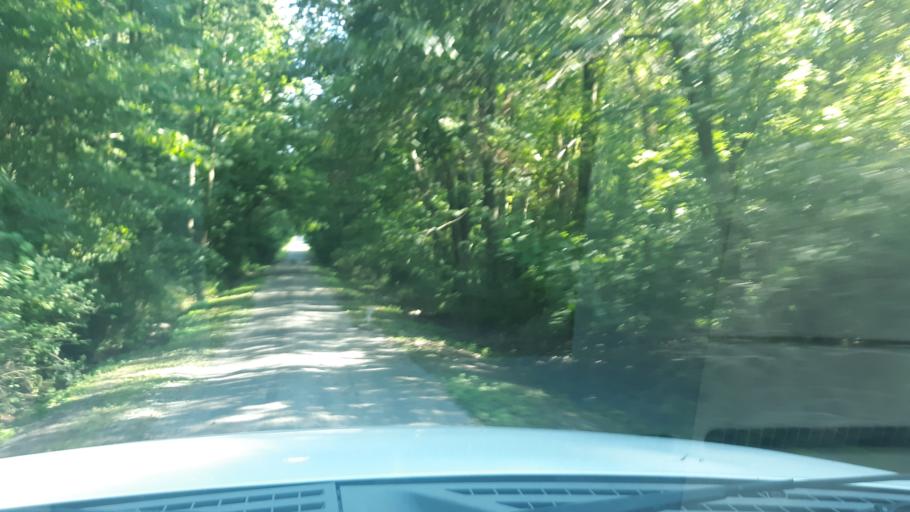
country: US
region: Illinois
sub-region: Saline County
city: Harrisburg
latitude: 37.8467
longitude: -88.6115
